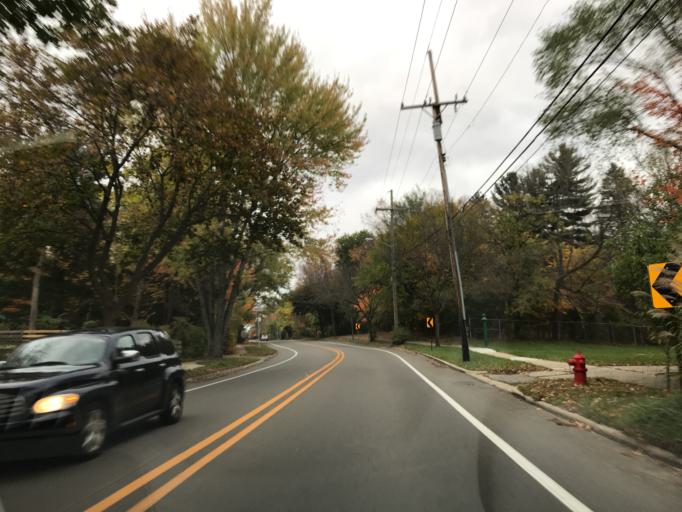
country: US
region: Michigan
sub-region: Washtenaw County
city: Ann Arbor
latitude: 42.3019
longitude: -83.7352
